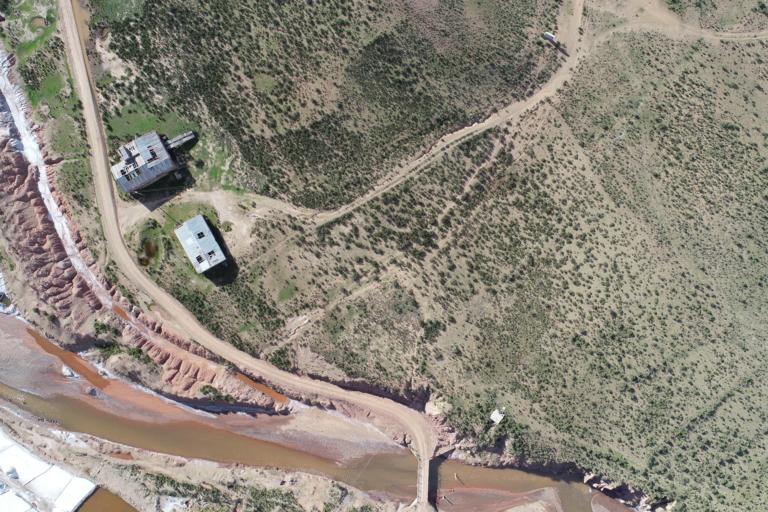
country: BO
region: La Paz
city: Patacamaya
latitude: -17.2980
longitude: -68.4838
